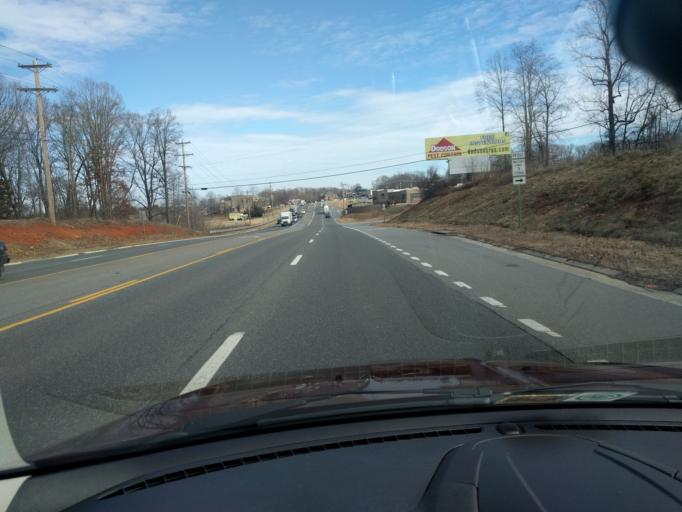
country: US
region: Virginia
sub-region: Bedford County
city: Forest
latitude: 37.3656
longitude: -79.2653
